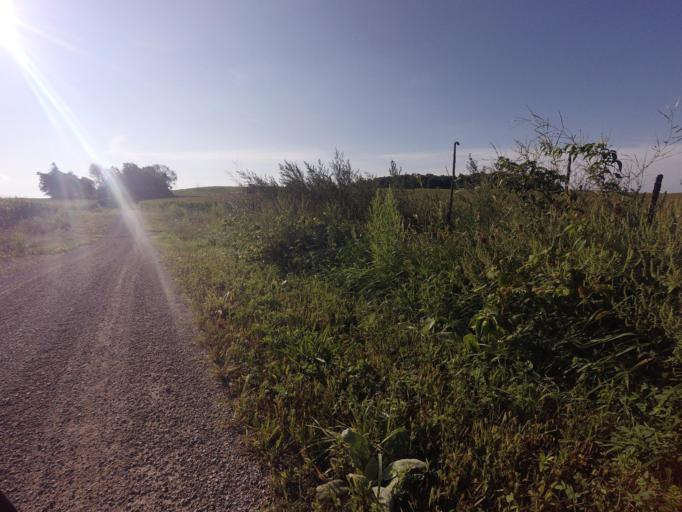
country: CA
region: Ontario
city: Goderich
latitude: 43.7445
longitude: -81.4917
